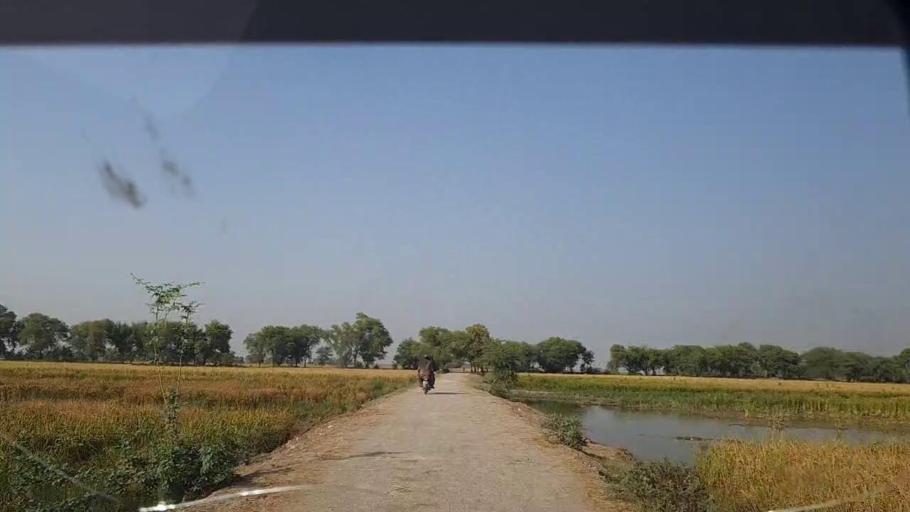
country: PK
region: Sindh
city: Shikarpur
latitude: 28.1219
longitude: 68.5831
